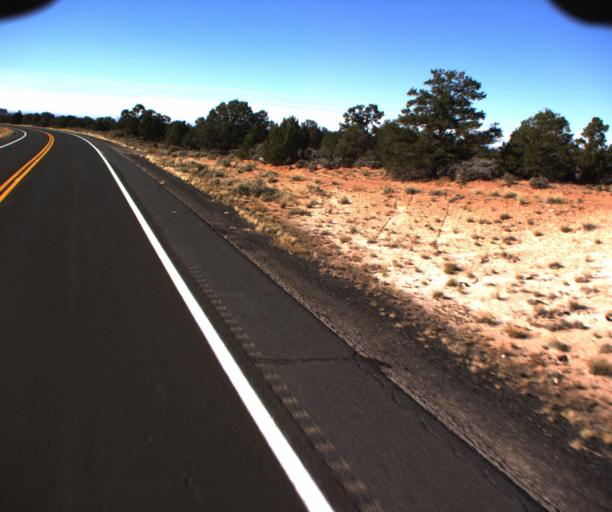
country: US
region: Arizona
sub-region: Coconino County
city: Kaibito
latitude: 36.5870
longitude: -110.8709
